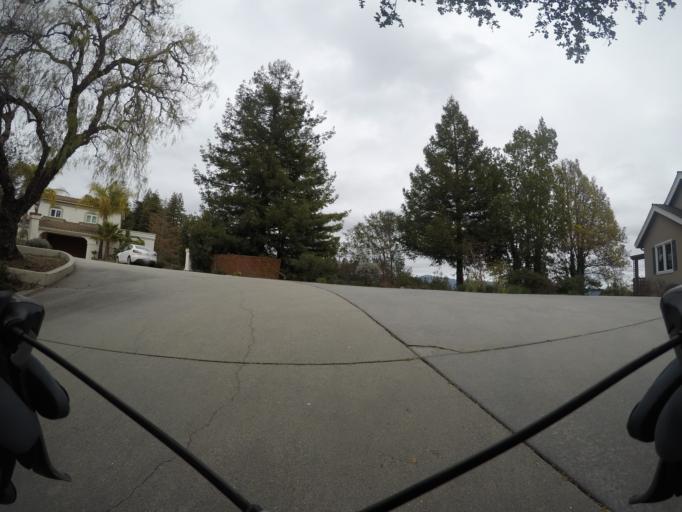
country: US
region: California
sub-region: Santa Cruz County
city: Scotts Valley
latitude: 37.0604
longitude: -121.9910
